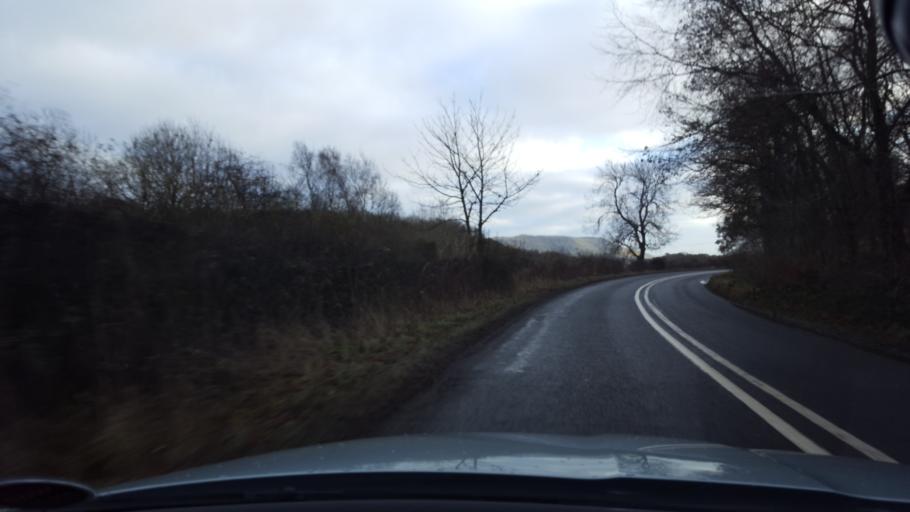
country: GB
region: Scotland
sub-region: Perth and Kinross
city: Milnathort
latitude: 56.2689
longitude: -3.3857
